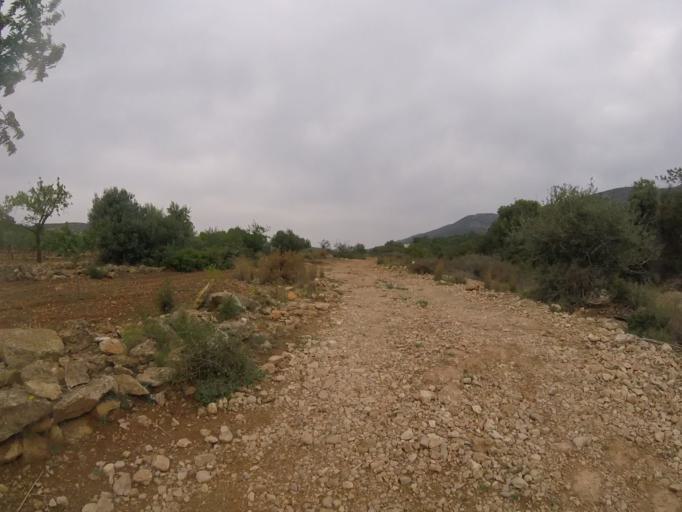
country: ES
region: Valencia
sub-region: Provincia de Castello
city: Alcala de Xivert
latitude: 40.2768
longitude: 0.2557
